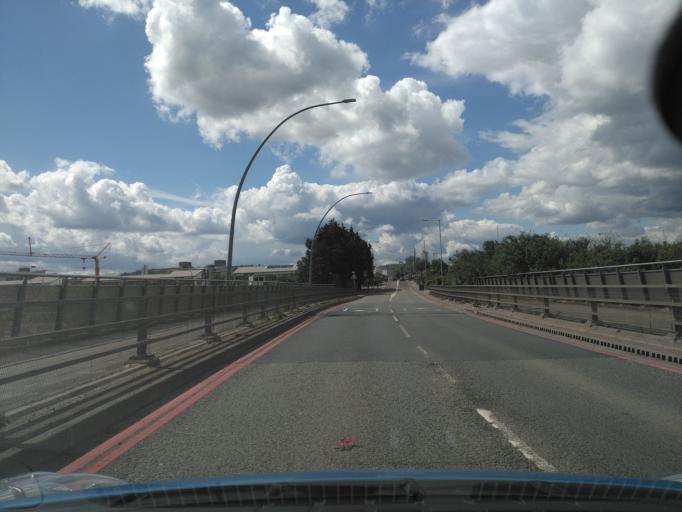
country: GB
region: England
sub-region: Greater London
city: Woolwich
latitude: 51.5047
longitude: 0.0712
